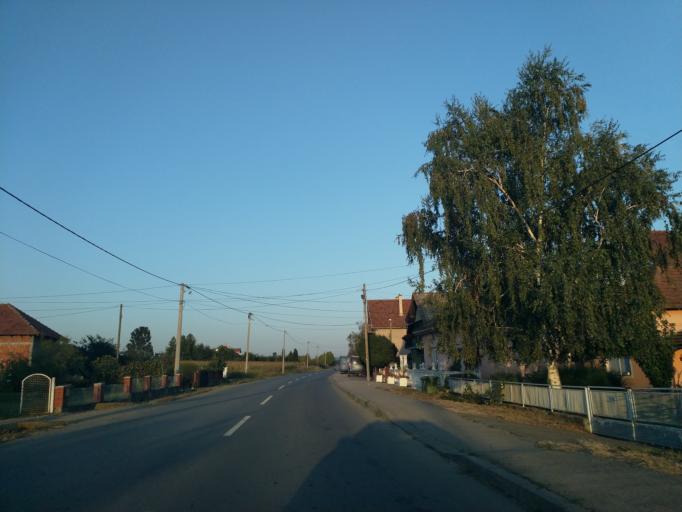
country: RS
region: Central Serbia
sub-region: Rasinski Okrug
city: Trstenik
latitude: 43.6301
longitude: 21.0862
